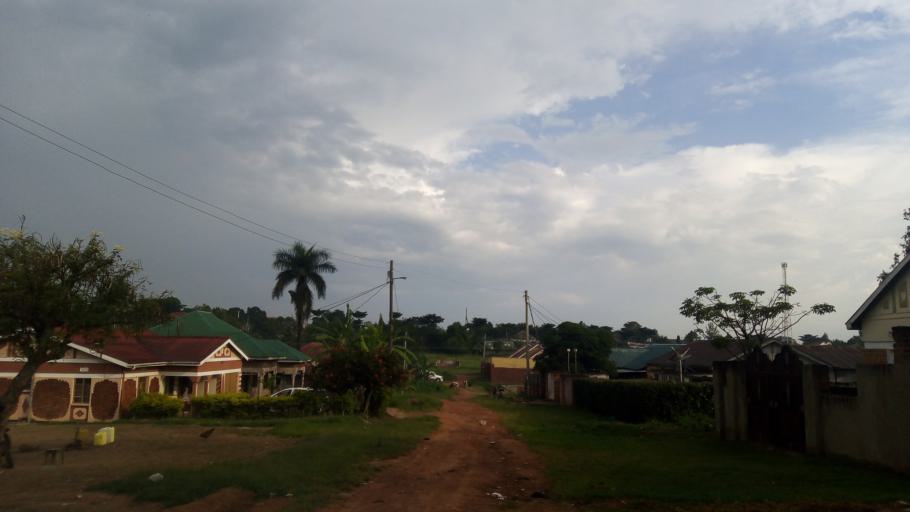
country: UG
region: Eastern Region
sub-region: Mbale District
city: Mbale
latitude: 1.0745
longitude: 34.1685
